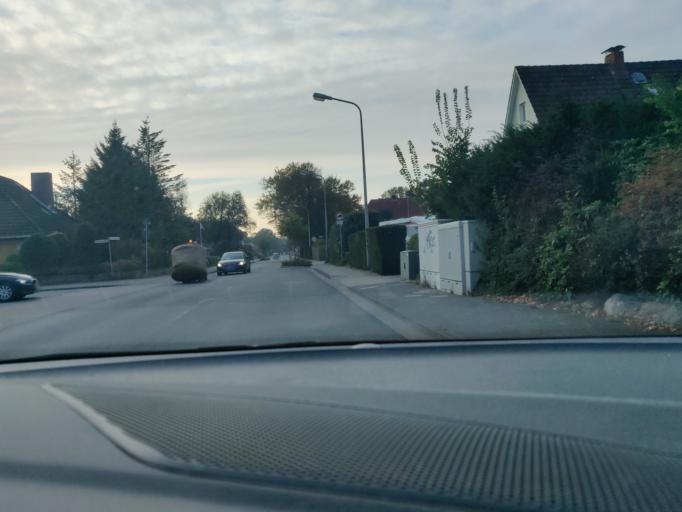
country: DE
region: Lower Saxony
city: Cuxhaven
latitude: 53.8612
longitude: 8.6297
